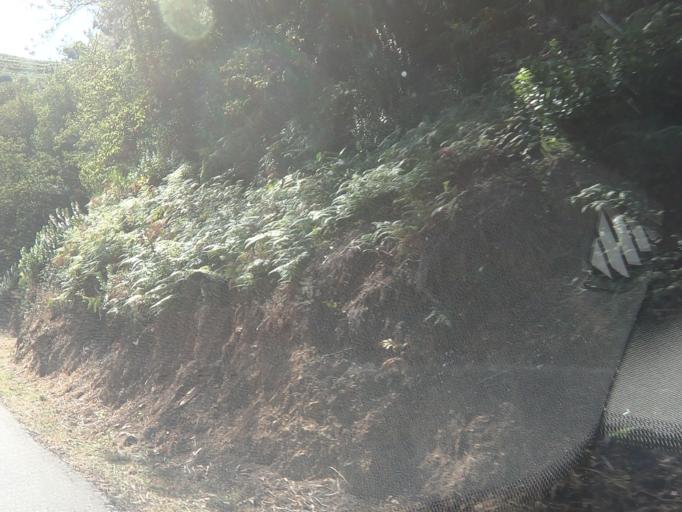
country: PT
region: Vila Real
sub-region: Santa Marta de Penaguiao
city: Santa Marta de Penaguiao
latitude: 41.2364
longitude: -7.7969
